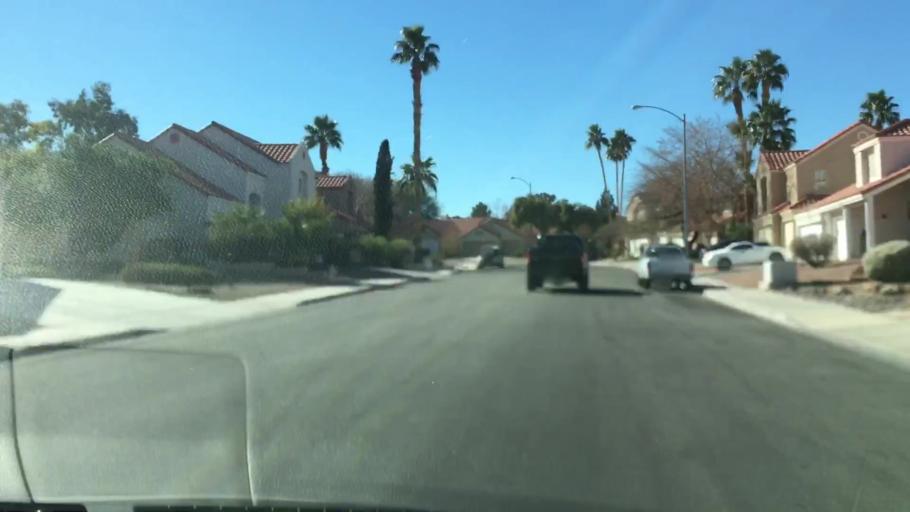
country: US
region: Nevada
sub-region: Clark County
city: Whitney
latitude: 36.0588
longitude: -115.0627
